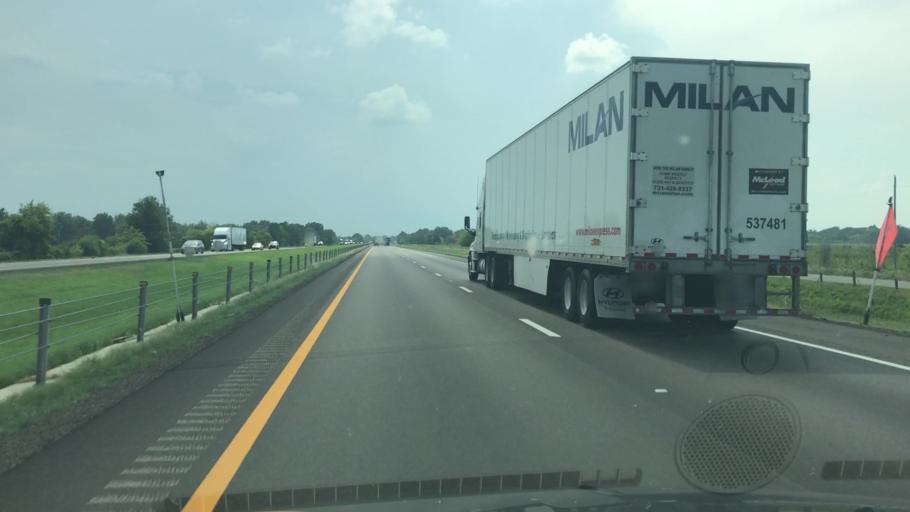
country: US
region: Arkansas
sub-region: Crittenden County
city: Earle
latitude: 35.1411
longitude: -90.4234
